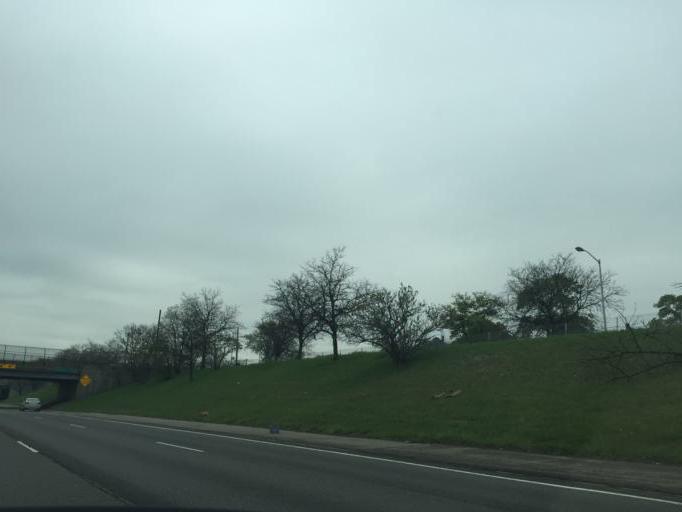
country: US
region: Michigan
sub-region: Wayne County
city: Highland Park
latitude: 42.3572
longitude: -83.1133
